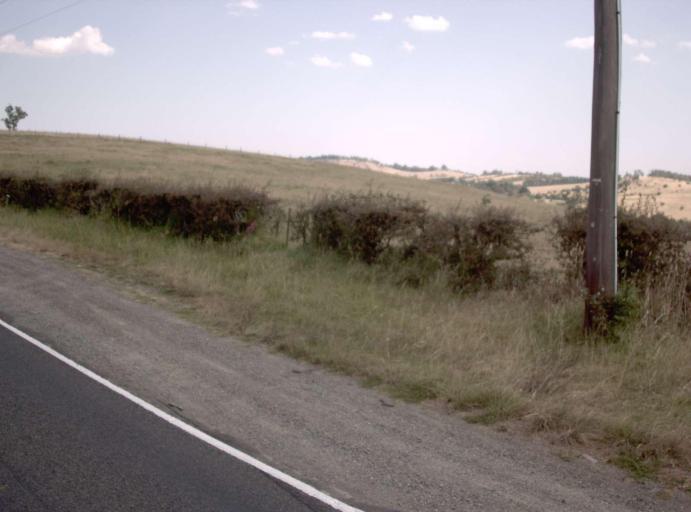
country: AU
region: Victoria
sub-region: Knox
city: Ferntree Gully
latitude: -37.9017
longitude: 145.2980
